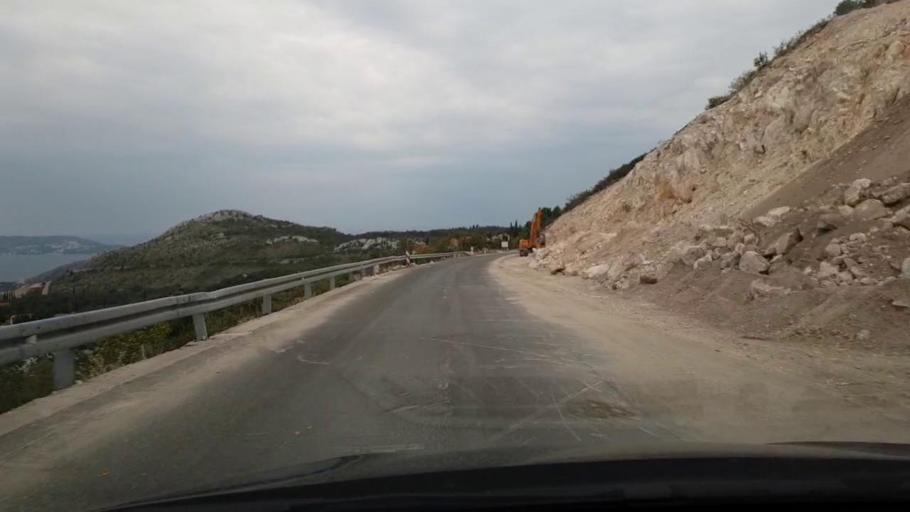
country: HR
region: Dubrovacko-Neretvanska
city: Cibaca
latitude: 42.6505
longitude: 18.1593
